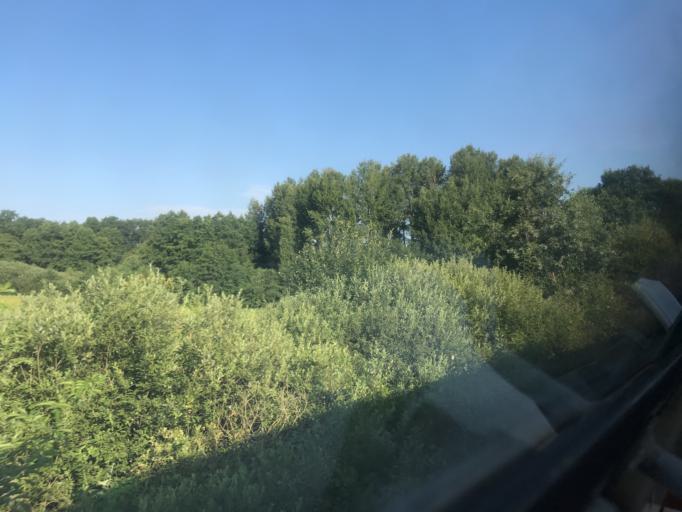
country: CZ
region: Jihocesky
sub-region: Okres Jindrichuv Hradec
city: Lomnice nad Luznici
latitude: 49.0679
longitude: 14.7349
